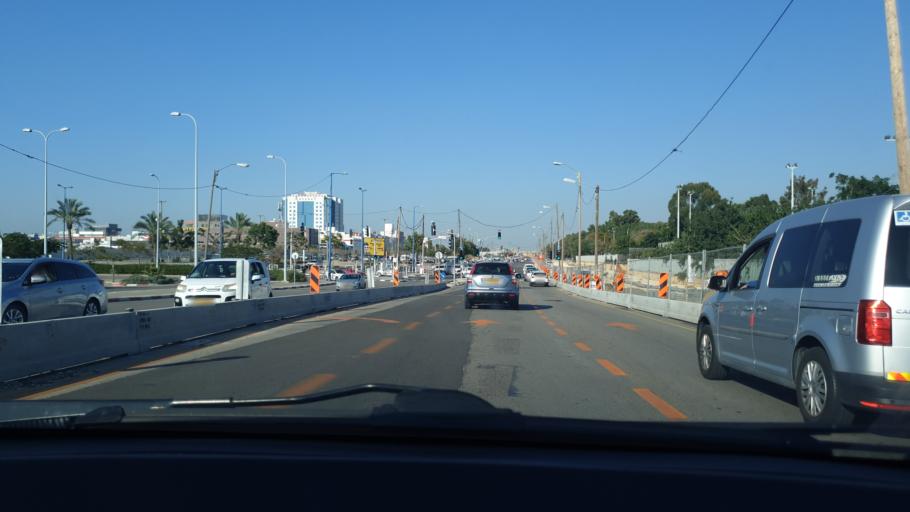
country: IL
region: Central District
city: Rishon LeZiyyon
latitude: 31.9829
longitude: 34.7723
